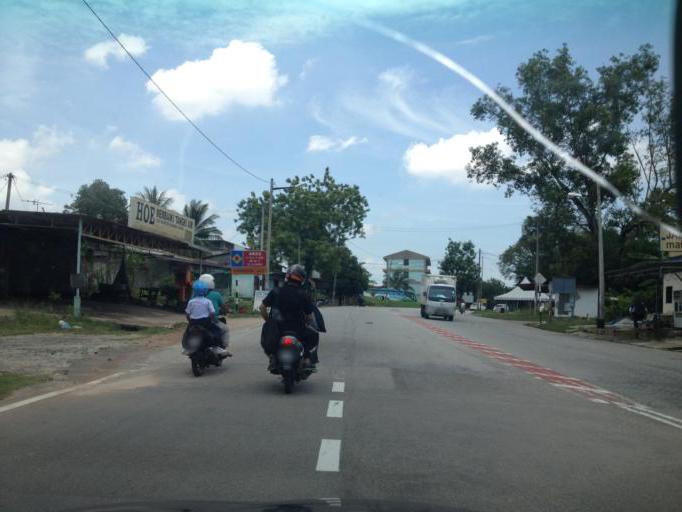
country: MY
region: Kedah
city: Sungai Petani
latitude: 5.6280
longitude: 100.5262
